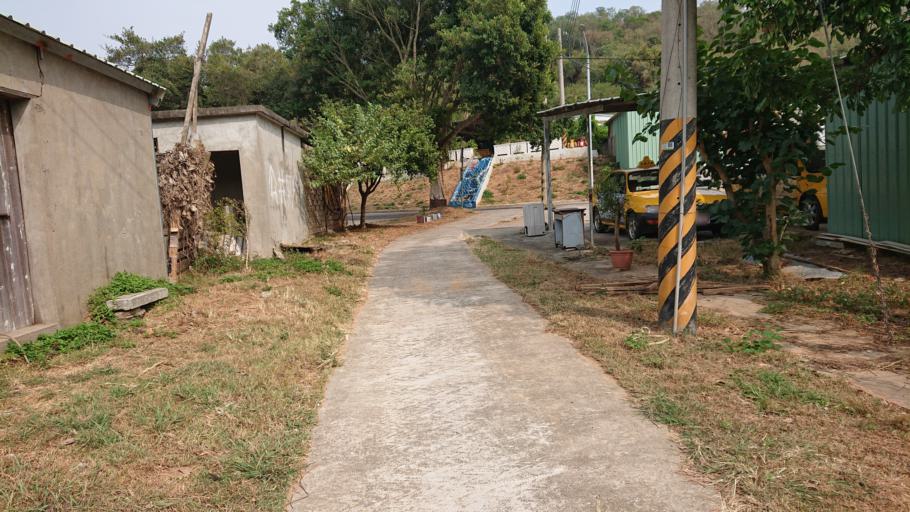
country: TW
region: Fukien
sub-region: Kinmen
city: Jincheng
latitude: 24.4318
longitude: 118.2472
